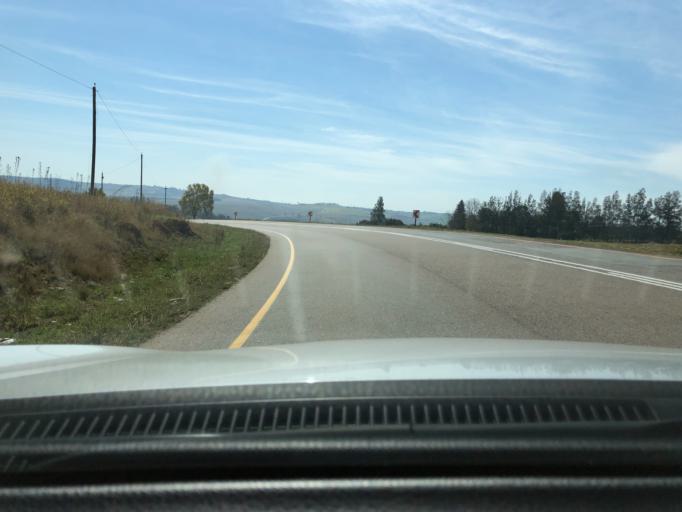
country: ZA
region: KwaZulu-Natal
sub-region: uMgungundlovu District Municipality
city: Richmond
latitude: -29.7950
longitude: 30.3496
